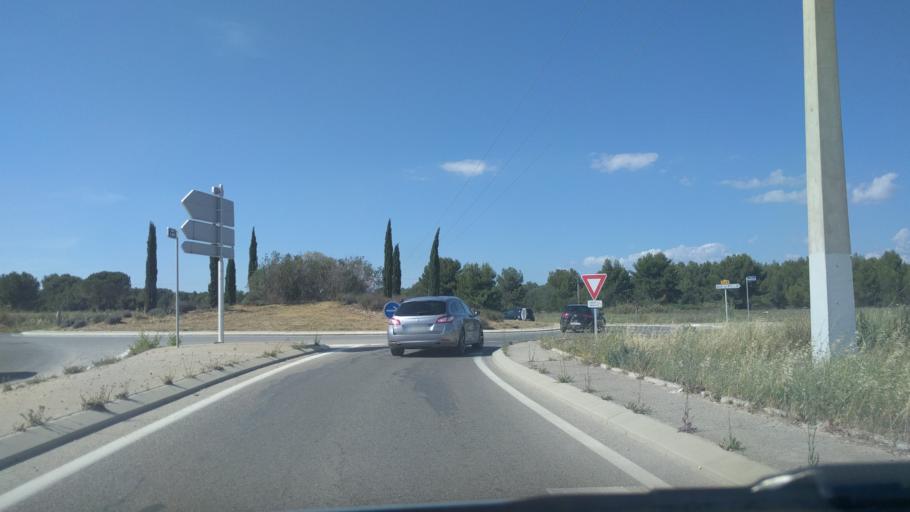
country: FR
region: Provence-Alpes-Cote d'Azur
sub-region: Departement des Bouches-du-Rhone
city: Eguilles
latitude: 43.5203
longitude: 5.3516
